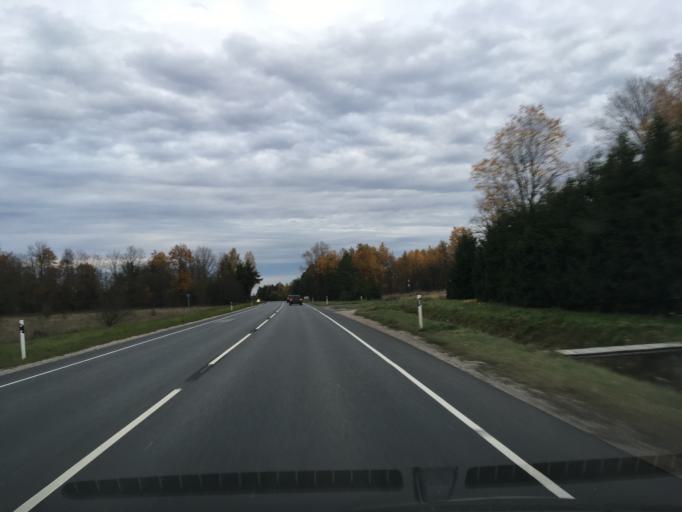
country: EE
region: Harju
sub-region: Nissi vald
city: Turba
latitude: 59.0897
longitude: 24.2441
